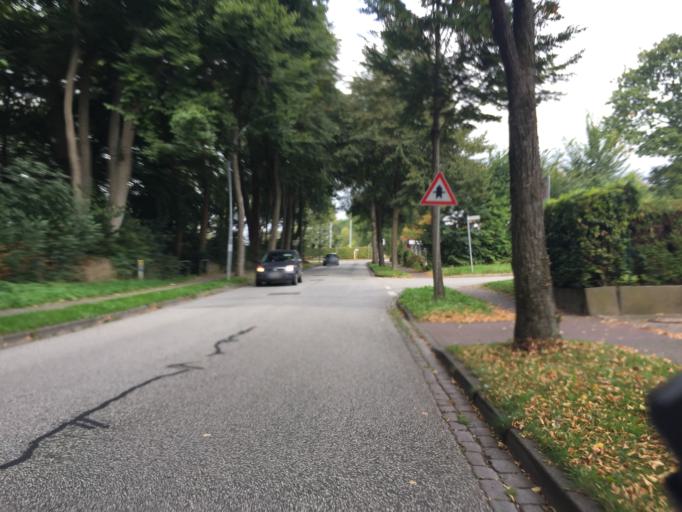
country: DE
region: Schleswig-Holstein
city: Itzehoe
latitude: 53.9304
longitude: 9.5384
